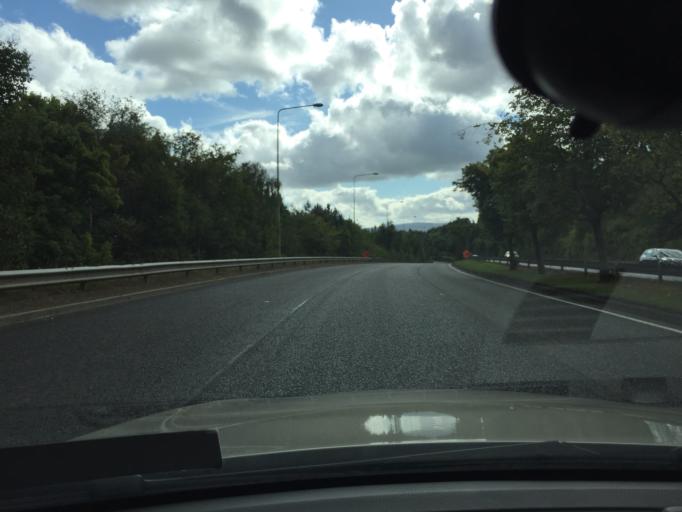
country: IE
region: Leinster
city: Chapelizod
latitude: 53.3489
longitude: -6.3493
